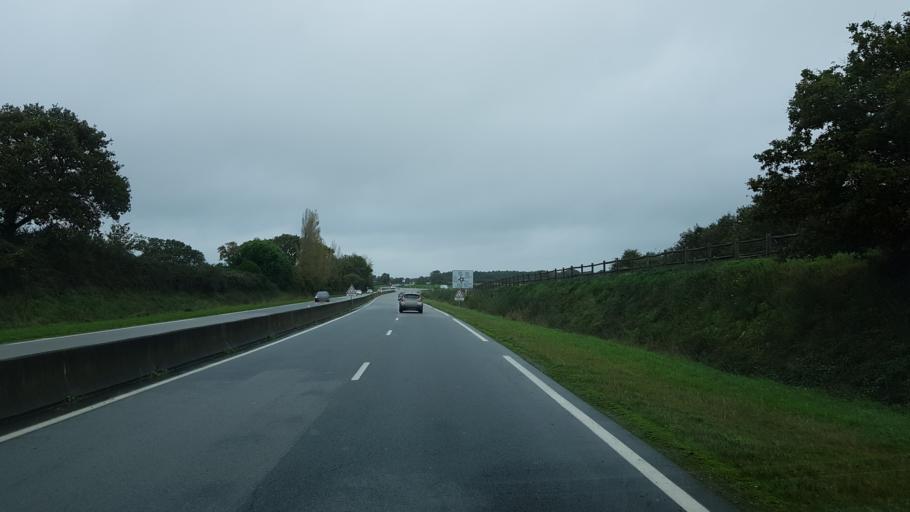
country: FR
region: Brittany
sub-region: Departement du Morbihan
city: Sarzeau
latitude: 47.5478
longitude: -2.7190
